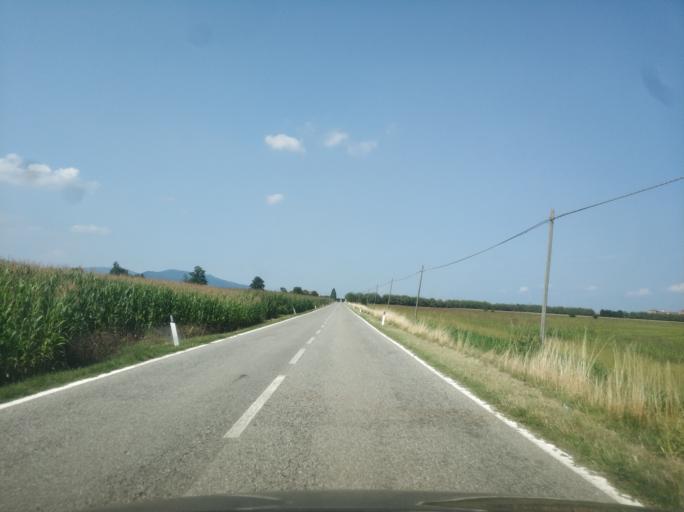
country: IT
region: Piedmont
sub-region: Provincia di Cuneo
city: Caraglio
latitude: 44.4445
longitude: 7.4541
